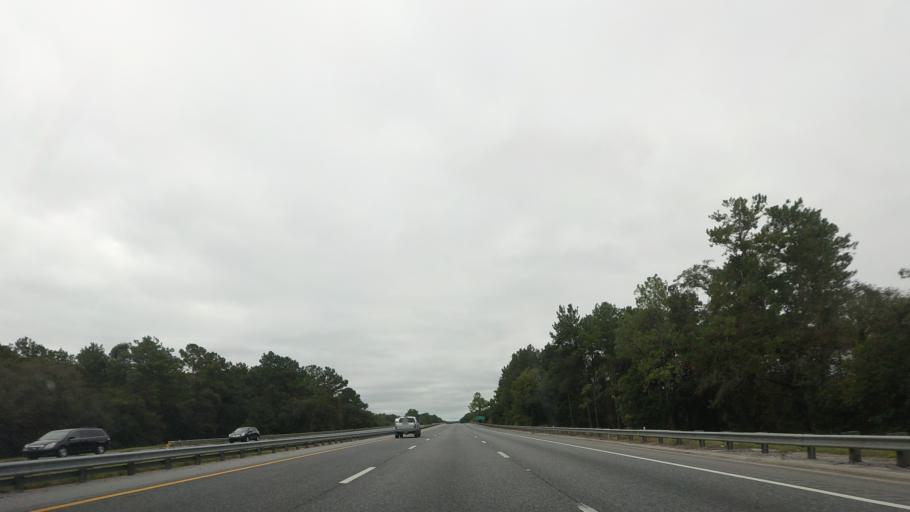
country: US
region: Florida
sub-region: Suwannee County
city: Wellborn
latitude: 30.3488
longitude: -82.8348
